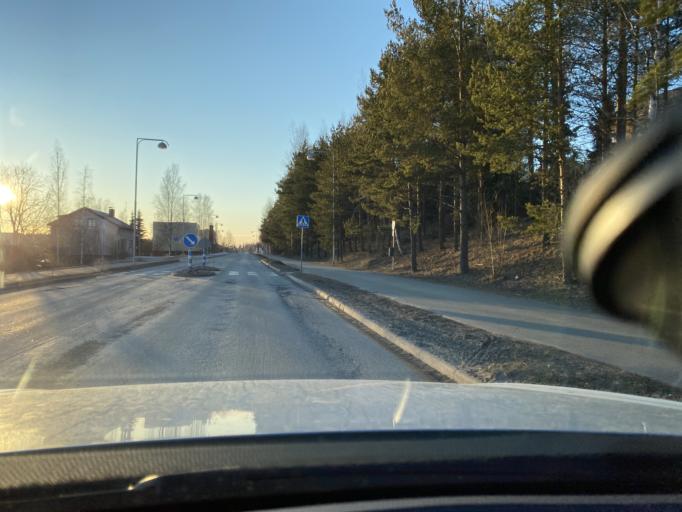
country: FI
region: Pirkanmaa
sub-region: Lounais-Pirkanmaa
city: Punkalaidun
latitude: 61.1103
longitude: 23.1145
